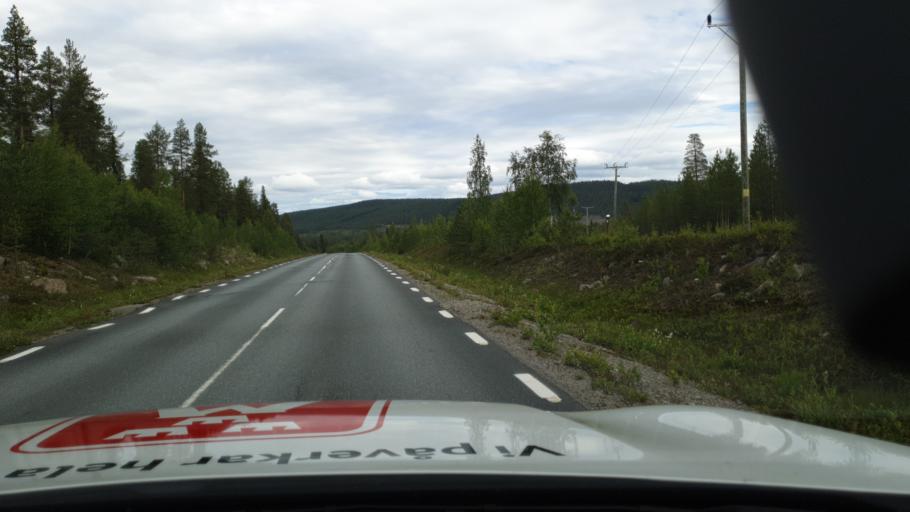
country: SE
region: Vaesterbotten
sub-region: Sorsele Kommun
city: Sorsele
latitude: 65.5334
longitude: 17.3946
